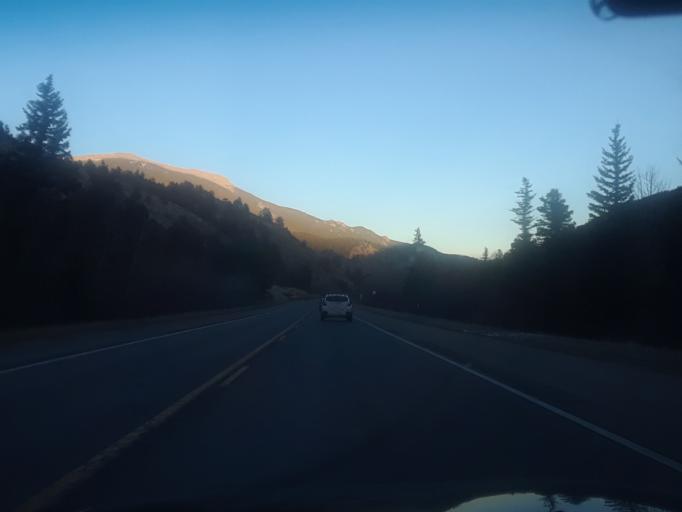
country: US
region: Colorado
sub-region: Clear Creek County
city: Georgetown
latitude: 39.4597
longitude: -105.7014
